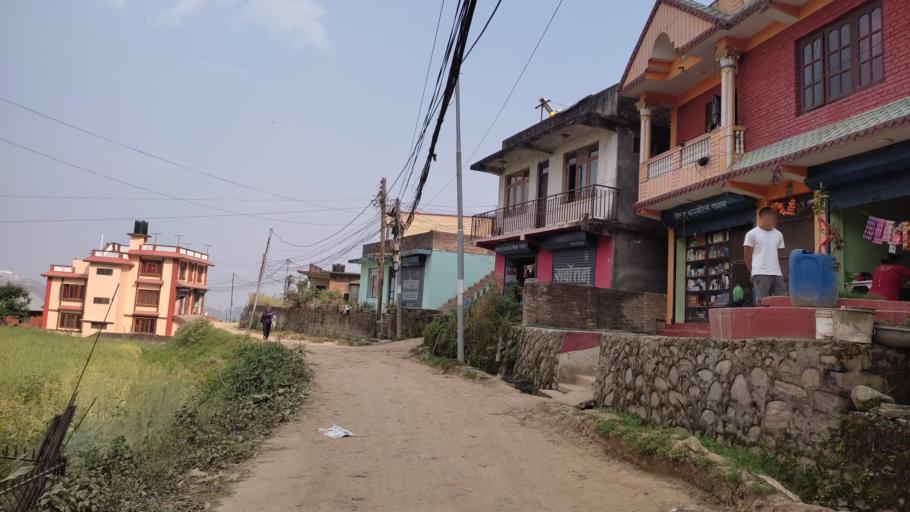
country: NP
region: Central Region
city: Kirtipur
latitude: 27.6608
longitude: 85.2592
